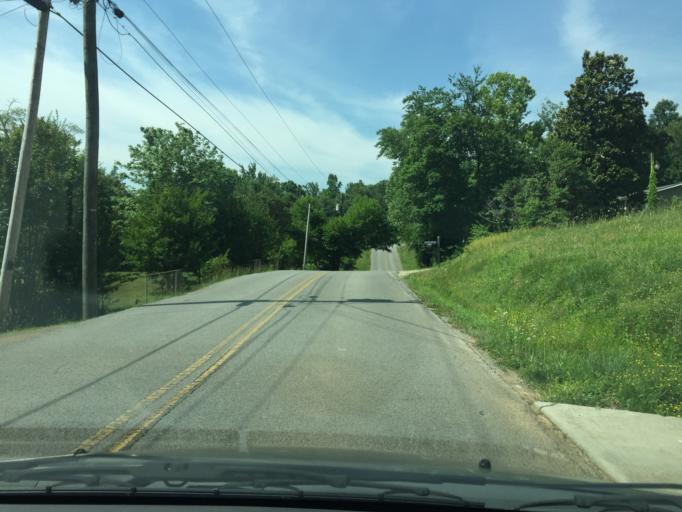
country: US
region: Tennessee
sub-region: Hamilton County
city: Collegedale
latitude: 35.0639
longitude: -85.0466
